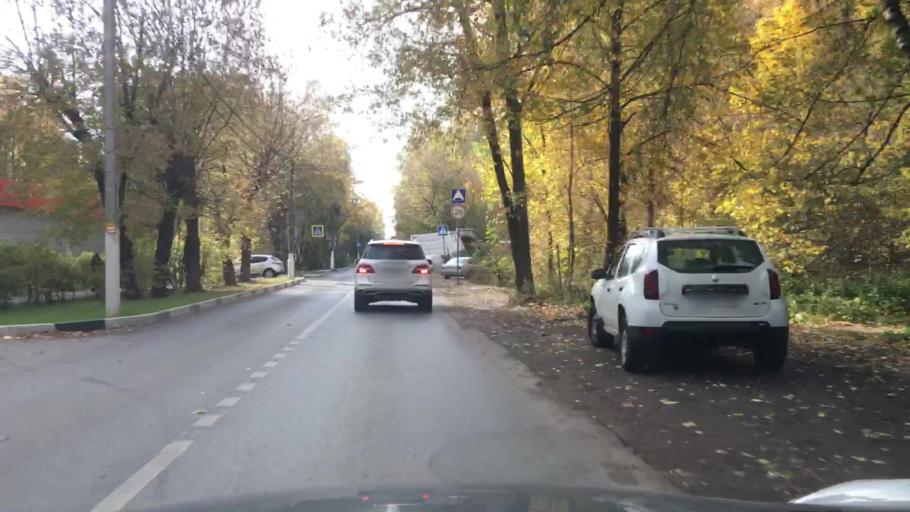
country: RU
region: Moskovskaya
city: Balashikha
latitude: 55.8023
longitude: 37.9272
